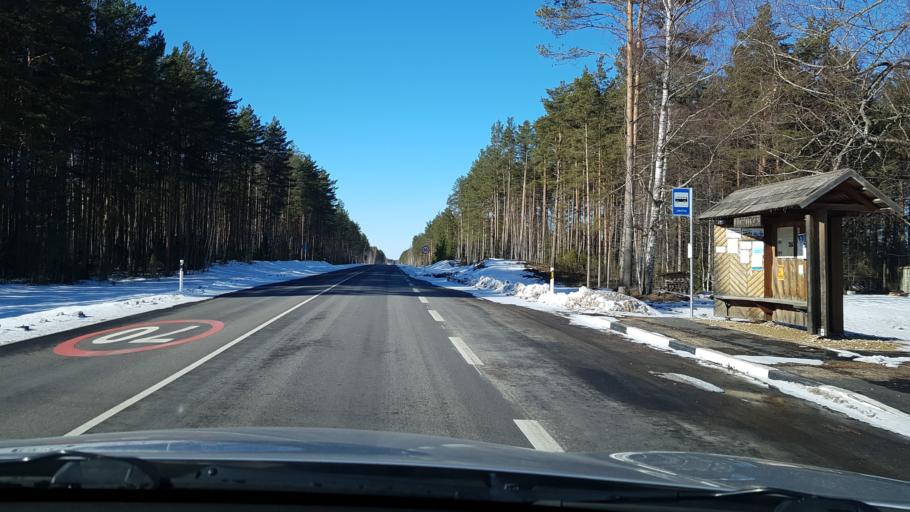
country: RU
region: Pskov
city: Pechory
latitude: 57.9591
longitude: 27.6176
